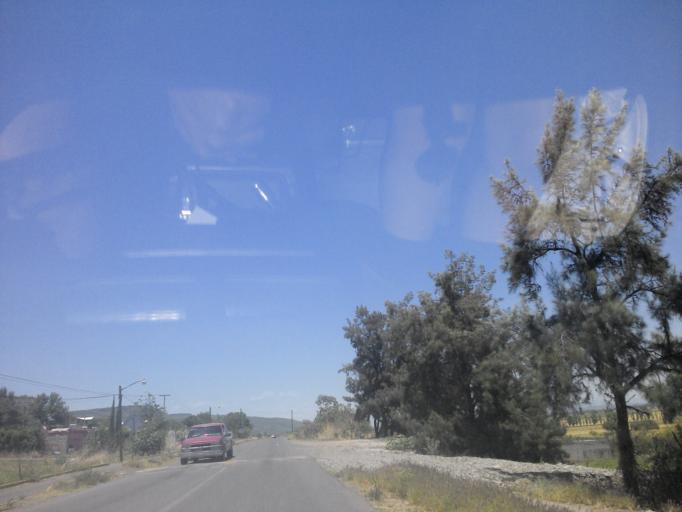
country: MX
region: Guanajuato
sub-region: San Francisco del Rincon
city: San Ignacio de Hidalgo
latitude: 20.9047
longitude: -101.9178
